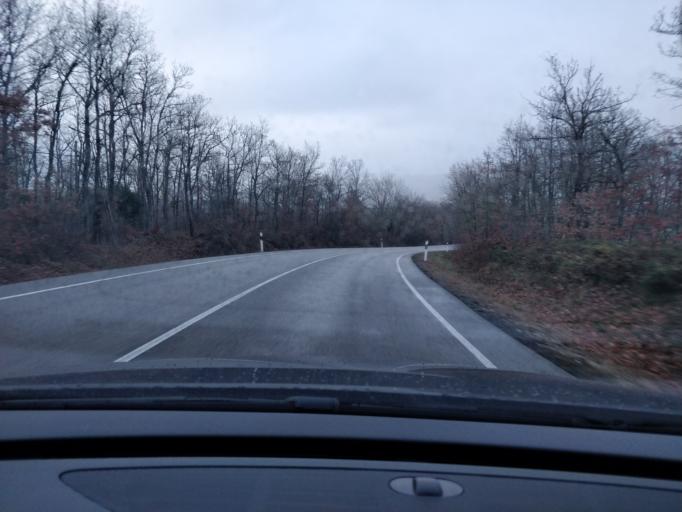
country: ES
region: Castille and Leon
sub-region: Provincia de Burgos
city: Espinosa de los Monteros
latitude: 43.0695
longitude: -3.5129
